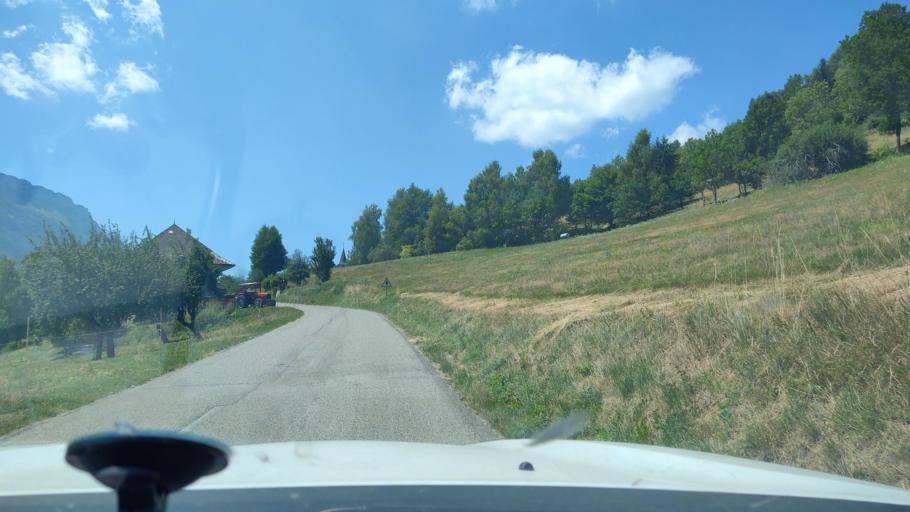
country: FR
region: Rhone-Alpes
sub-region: Departement de la Haute-Savoie
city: Cusy
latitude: 45.6845
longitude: 6.0588
